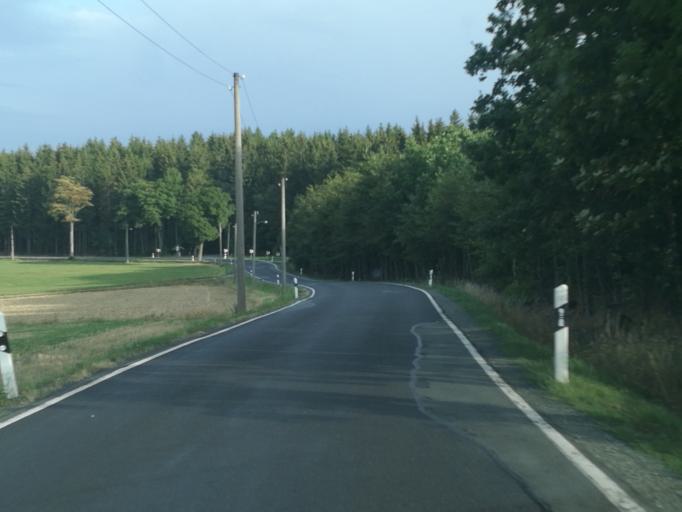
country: DE
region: Saxony
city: Triebel
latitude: 50.3337
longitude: 12.1192
